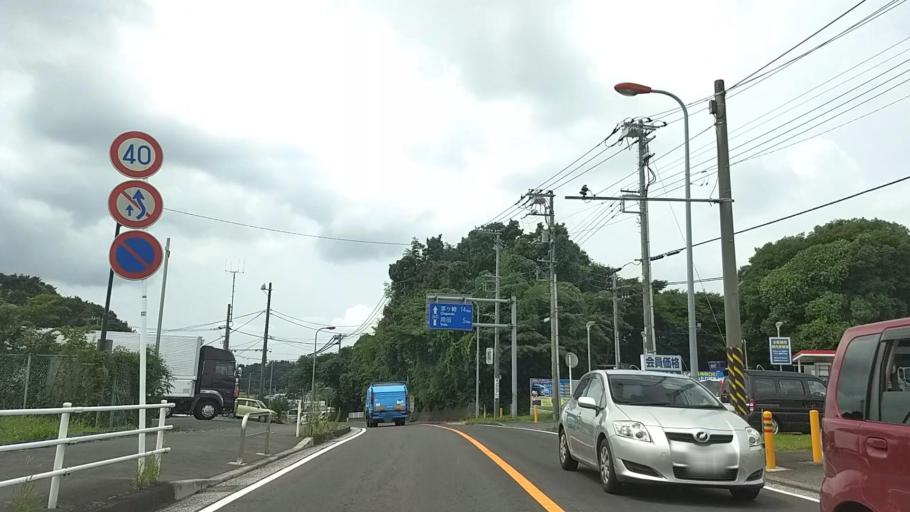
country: JP
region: Kanagawa
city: Minami-rinkan
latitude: 35.4398
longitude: 139.4473
